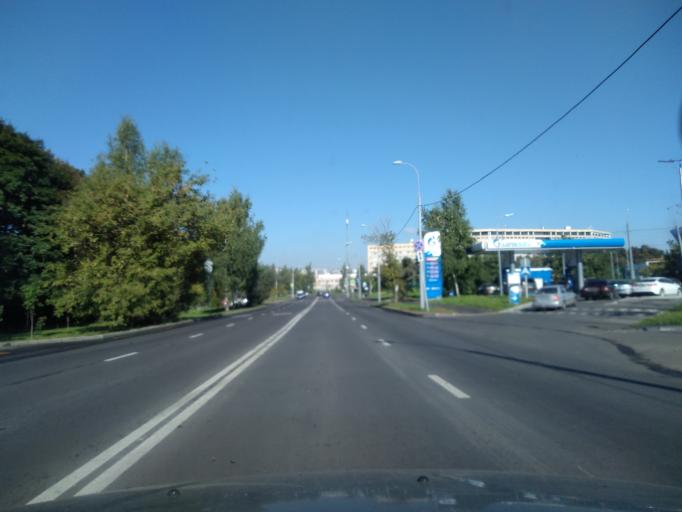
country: RU
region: Moscow
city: Strogino
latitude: 55.8487
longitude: 37.4033
